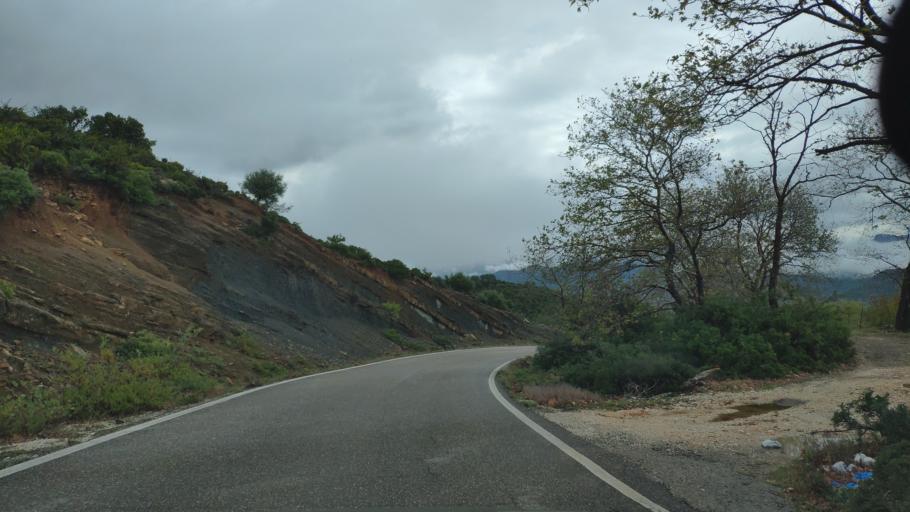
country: GR
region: West Greece
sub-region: Nomos Aitolias kai Akarnanias
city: Sardinia
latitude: 38.8467
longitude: 21.3183
